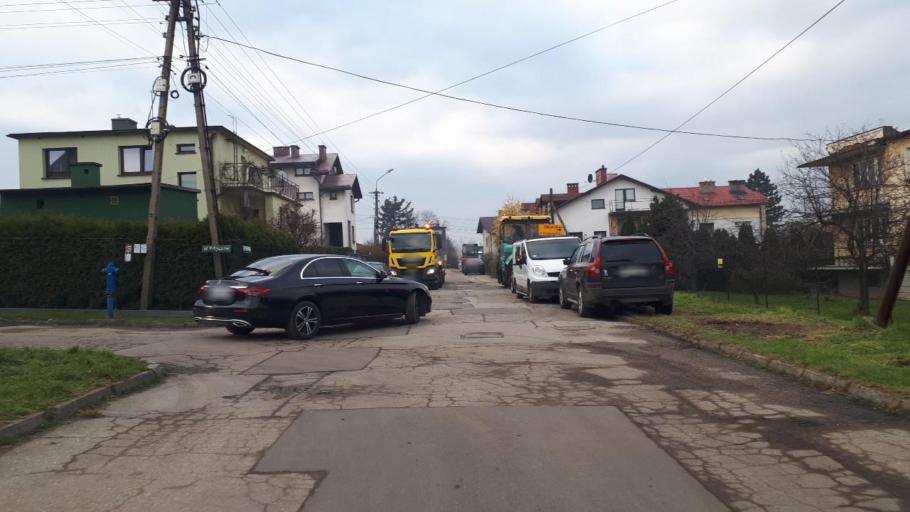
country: PL
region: Silesian Voivodeship
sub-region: Powiat bielski
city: Kozy
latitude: 49.8460
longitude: 19.1483
